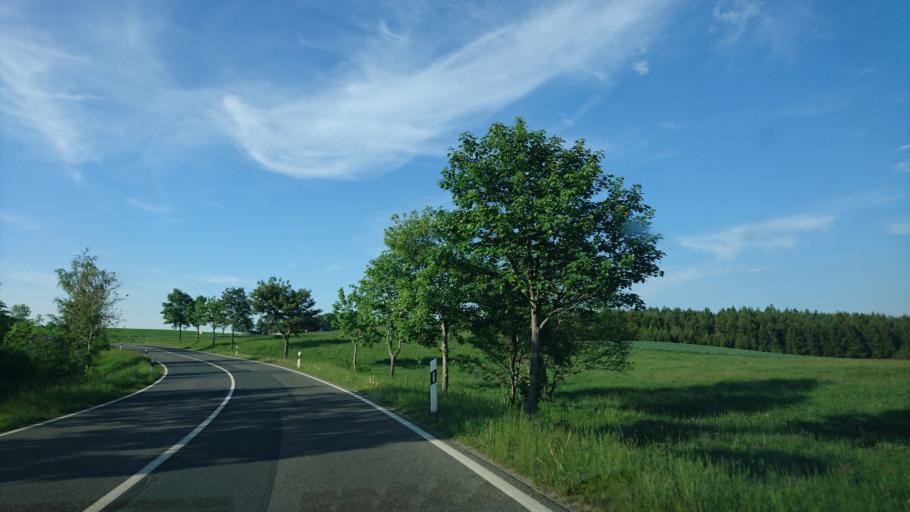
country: DE
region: Saxony
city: Stutzengrun
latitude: 50.5365
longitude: 12.5319
